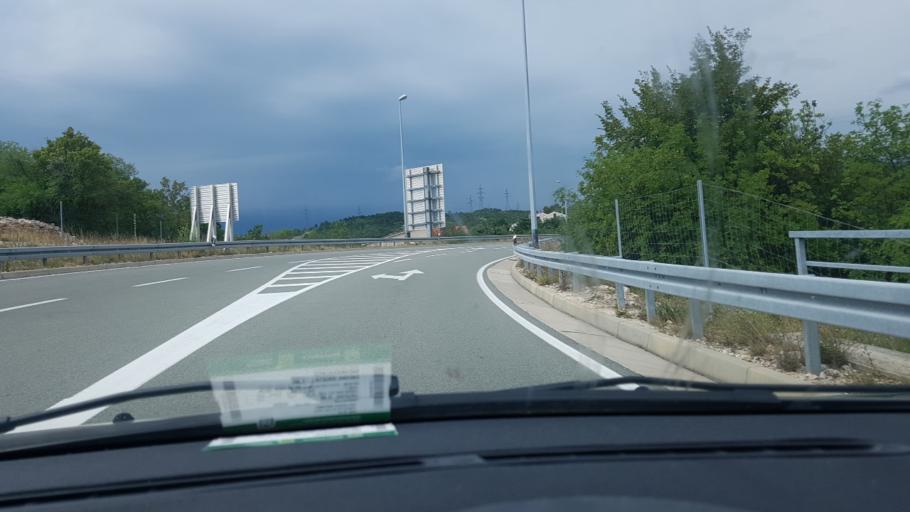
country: HR
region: Primorsko-Goranska
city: Hreljin
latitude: 45.2927
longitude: 14.5875
